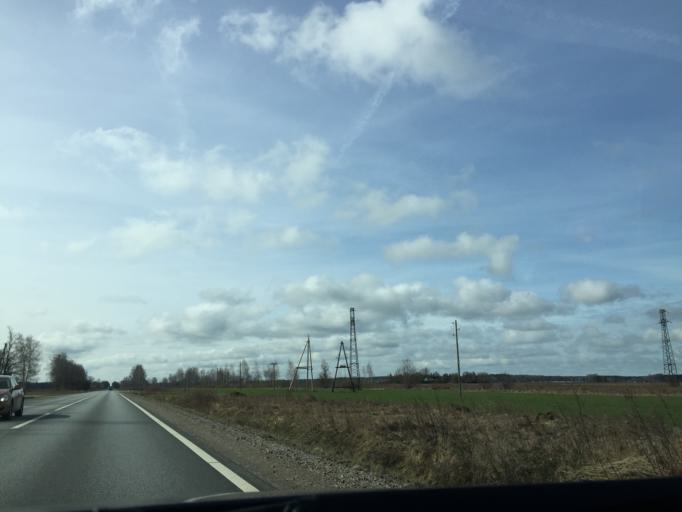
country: LV
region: Jelgava
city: Jelgava
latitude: 56.4402
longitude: 23.6882
